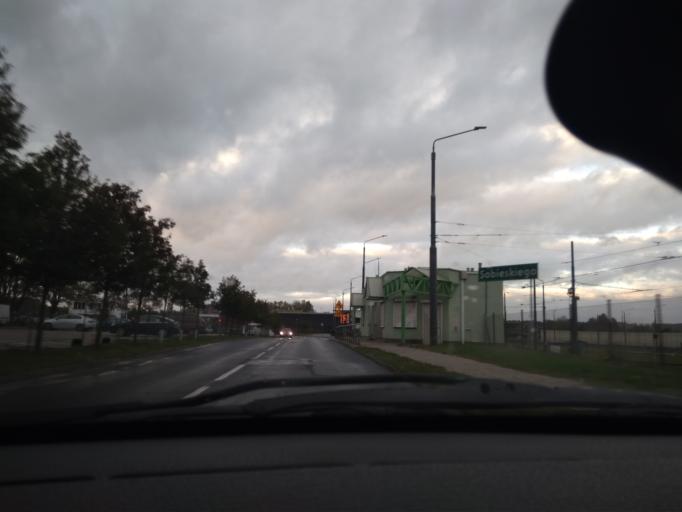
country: PL
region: Greater Poland Voivodeship
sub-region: Powiat poznanski
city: Suchy Las
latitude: 52.4630
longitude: 16.9165
